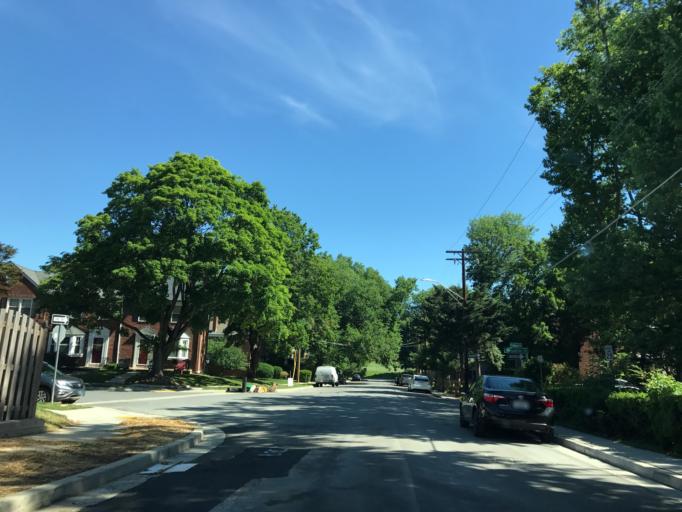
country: US
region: Maryland
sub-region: Baltimore County
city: Towson
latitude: 39.3783
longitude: -76.6138
